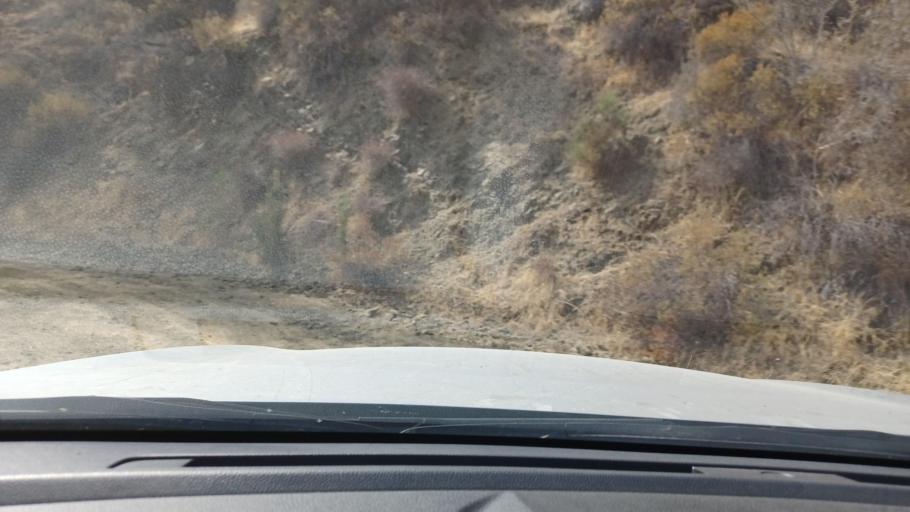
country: CY
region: Pafos
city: Polis
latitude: 35.0211
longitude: 32.5343
